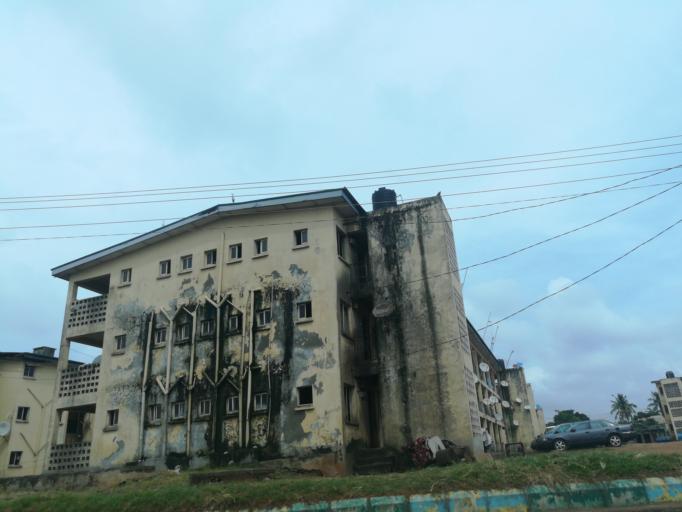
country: NG
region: Lagos
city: Ojota
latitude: 6.5719
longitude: 3.3612
